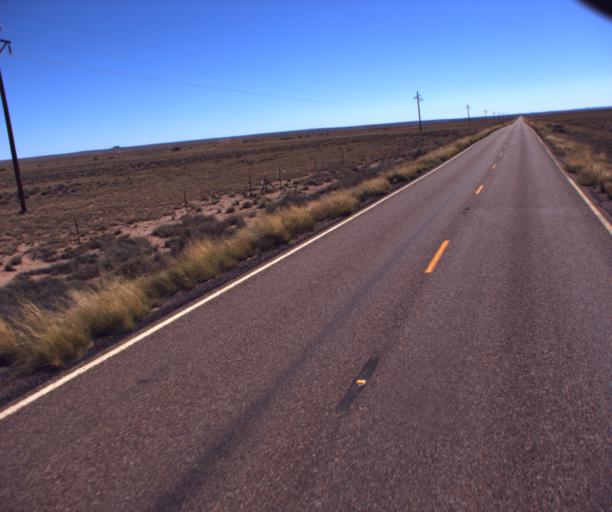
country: US
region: Arizona
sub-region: Navajo County
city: Holbrook
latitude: 35.1307
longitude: -110.0912
